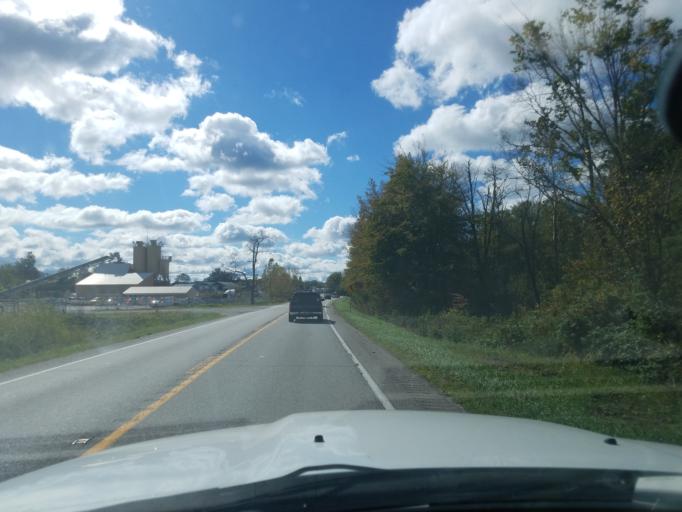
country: US
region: Kentucky
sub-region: Laurel County
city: London
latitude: 37.0717
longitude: -84.0585
